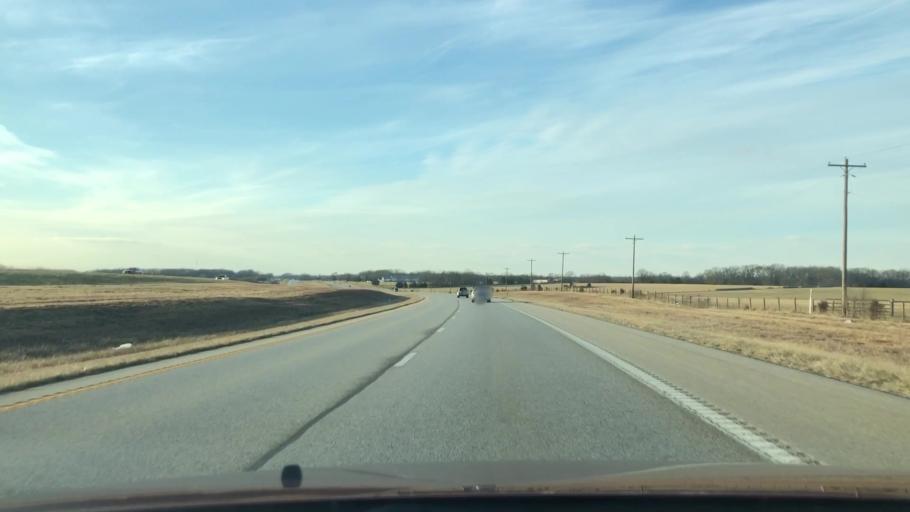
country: US
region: Missouri
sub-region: Webster County
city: Seymour
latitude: 37.1228
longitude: -92.6994
